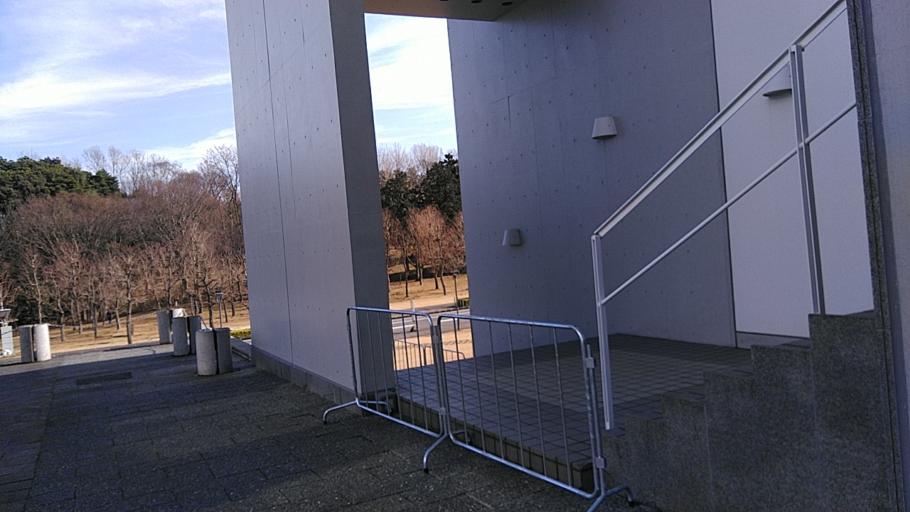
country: JP
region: Kanagawa
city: Fujisawa
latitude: 35.3881
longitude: 139.4279
